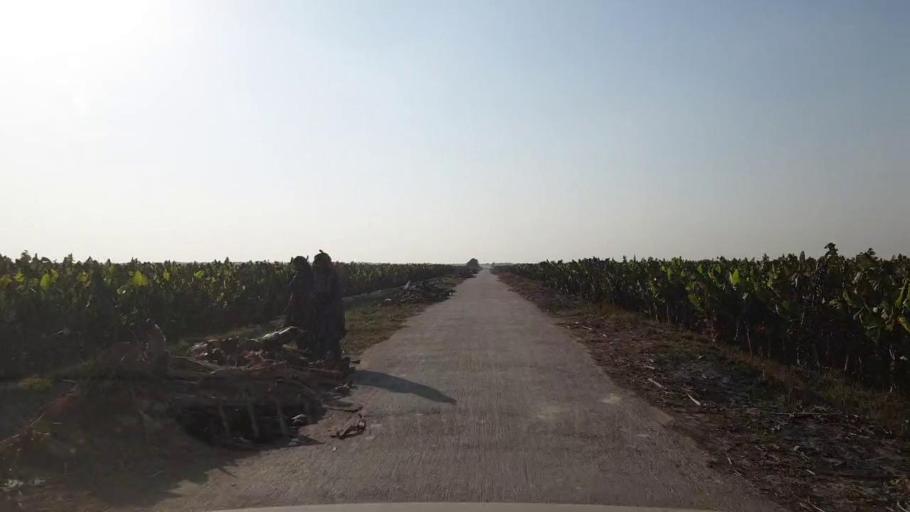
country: PK
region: Sindh
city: Tando Allahyar
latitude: 25.3467
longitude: 68.6786
